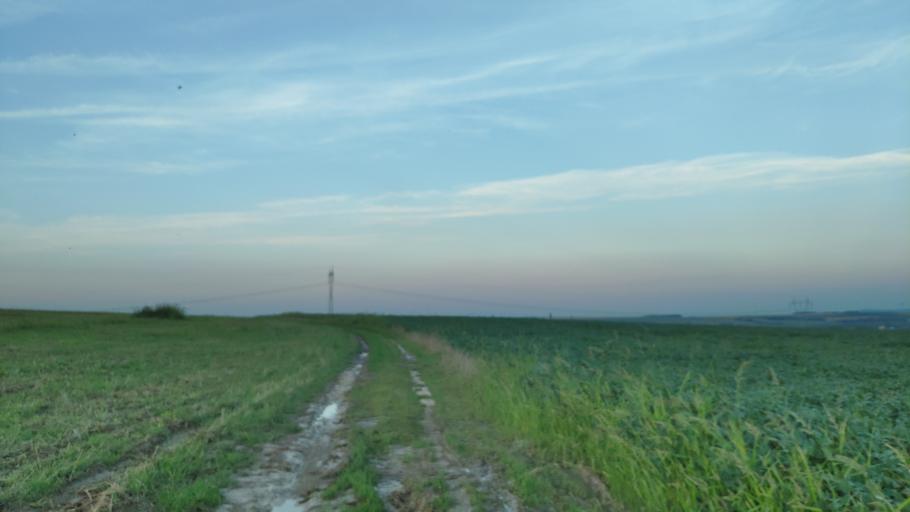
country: SK
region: Kosicky
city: Secovce
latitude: 48.5919
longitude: 21.5381
